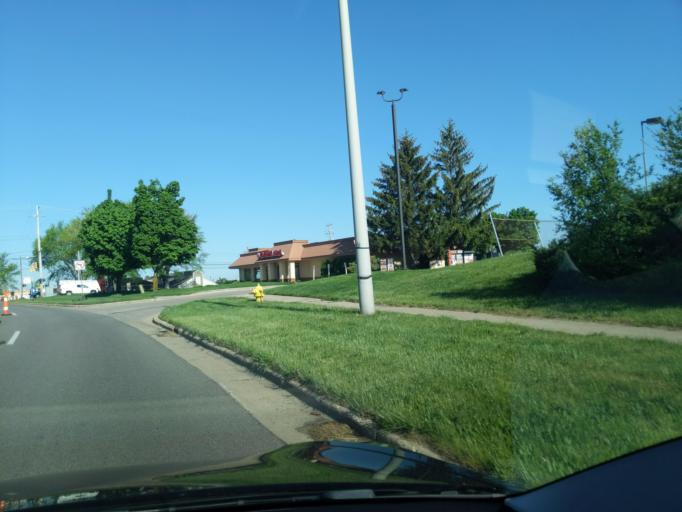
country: US
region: Michigan
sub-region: Kent County
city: East Grand Rapids
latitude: 42.9106
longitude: -85.5671
